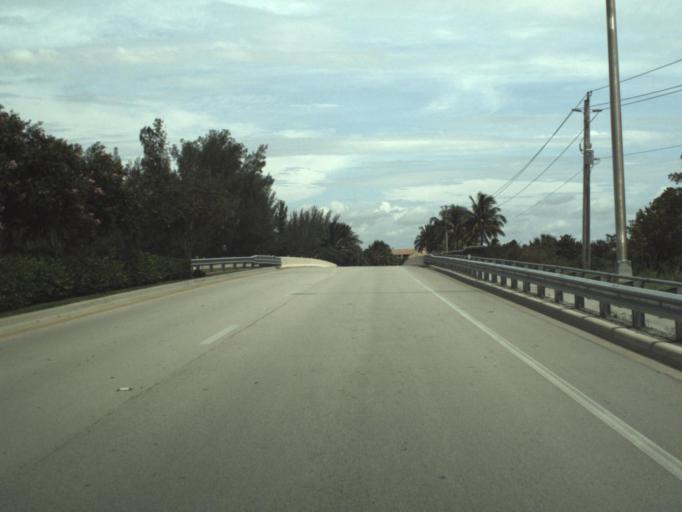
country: US
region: Florida
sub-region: Palm Beach County
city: Jupiter
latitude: 26.9367
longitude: -80.0823
